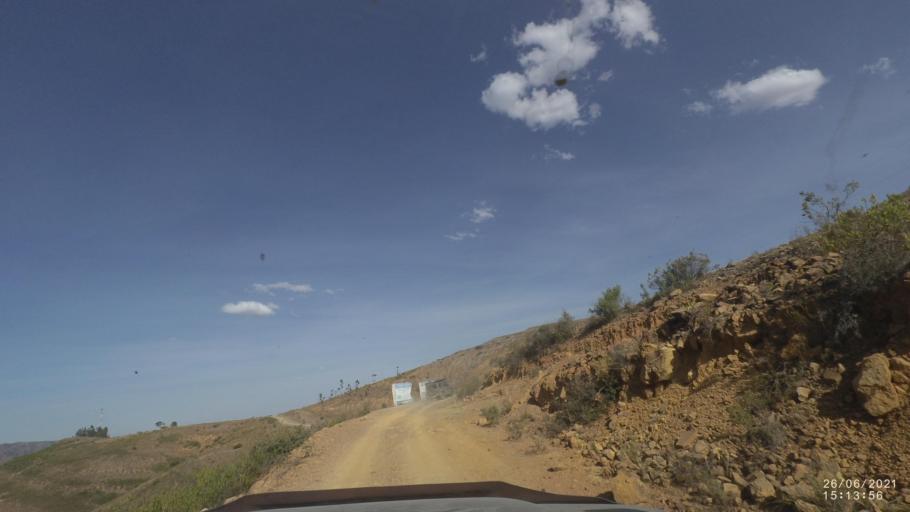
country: BO
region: Cochabamba
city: Mizque
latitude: -17.9612
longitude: -65.6426
